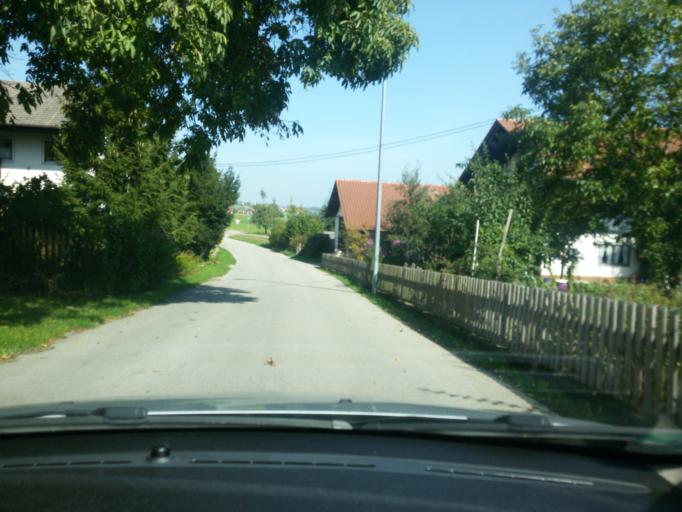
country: DE
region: Bavaria
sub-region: Swabia
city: Scherstetten
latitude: 48.1835
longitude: 10.6397
